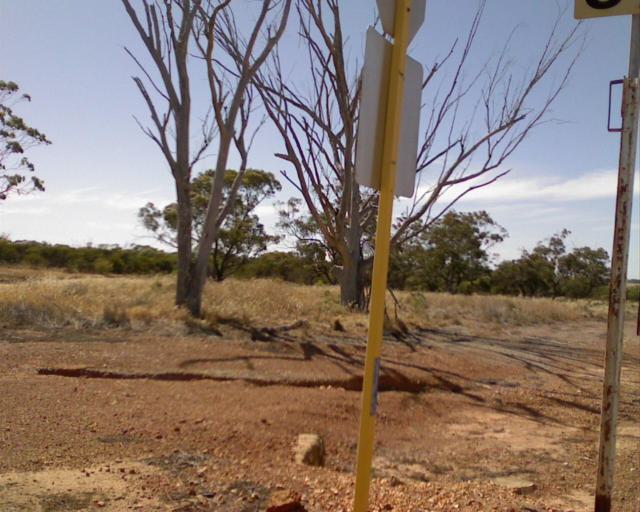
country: AU
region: Western Australia
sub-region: Moora
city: Moora
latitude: -30.1504
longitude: 116.0845
